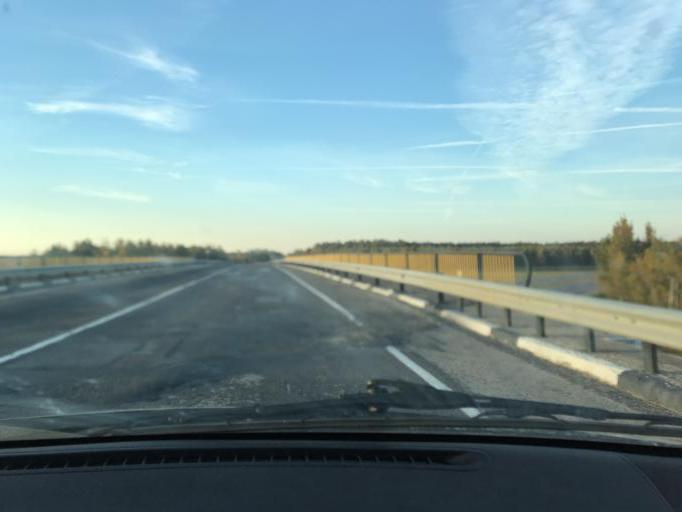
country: BY
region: Brest
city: Horad Kobryn
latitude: 52.2233
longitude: 24.4238
